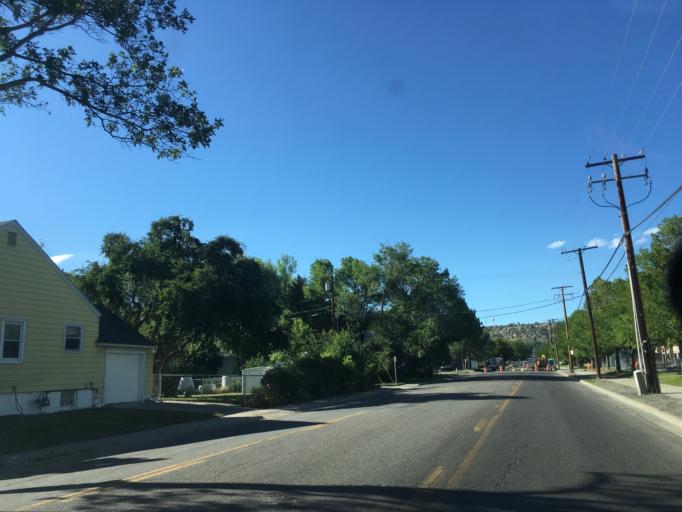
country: US
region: Montana
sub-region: Yellowstone County
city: Billings
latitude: 45.7851
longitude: -108.5588
